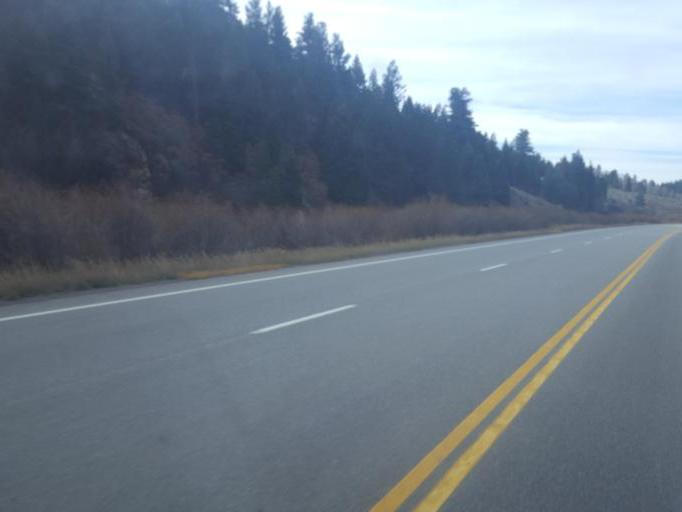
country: US
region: Colorado
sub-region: Costilla County
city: San Luis
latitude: 37.5730
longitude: -105.2763
